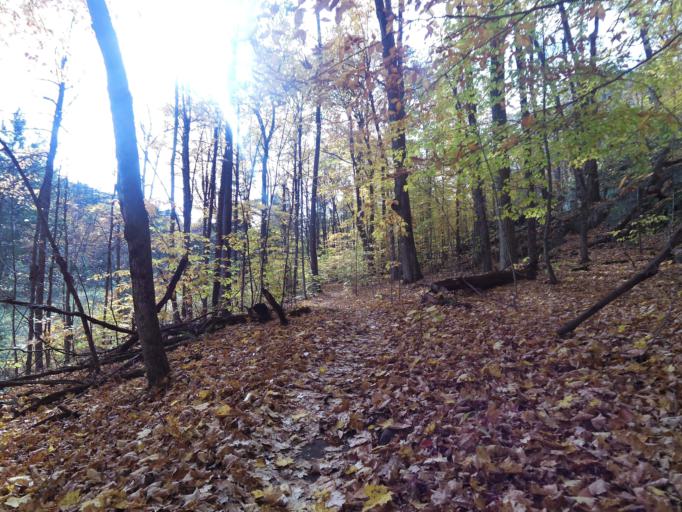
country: CA
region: Quebec
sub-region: Outaouais
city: Gatineau
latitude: 45.4810
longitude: -75.8174
